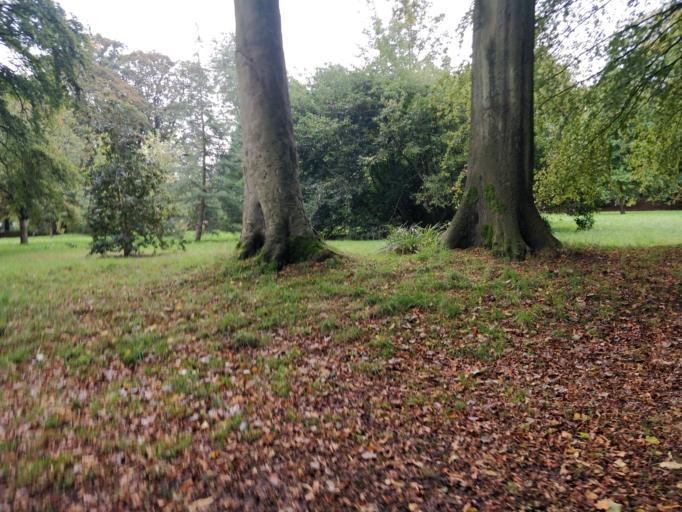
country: GB
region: England
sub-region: Lancashire
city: Banks
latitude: 53.6636
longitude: -2.9597
